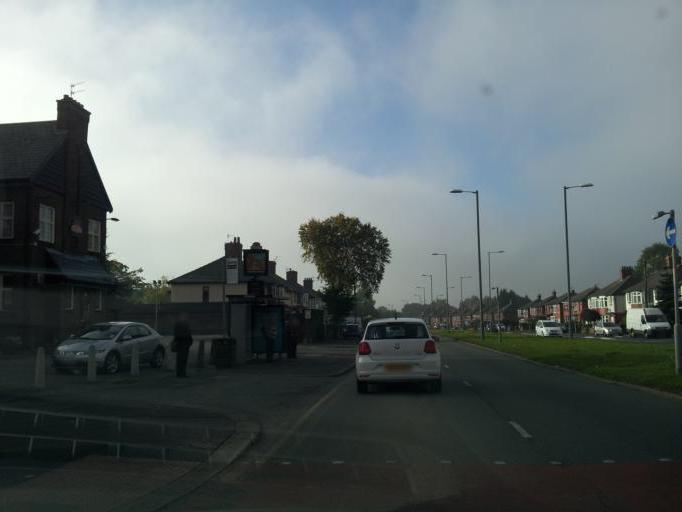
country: GB
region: England
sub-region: Manchester
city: Failsworth
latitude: 53.5167
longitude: -2.1687
